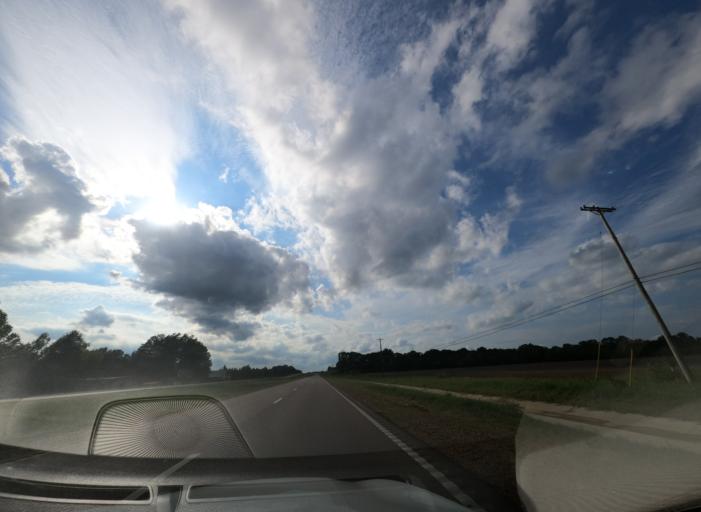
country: US
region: Tennessee
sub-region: Fayette County
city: Piperton
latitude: 34.9799
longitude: -89.5794
